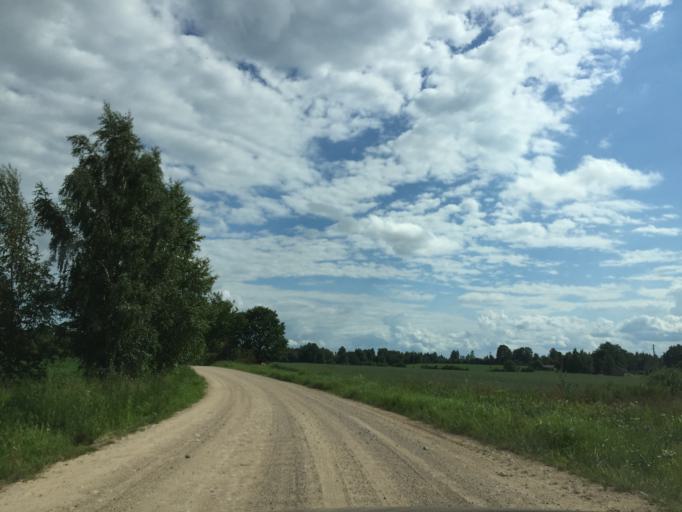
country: LV
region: Malpils
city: Malpils
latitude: 56.8508
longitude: 25.0489
